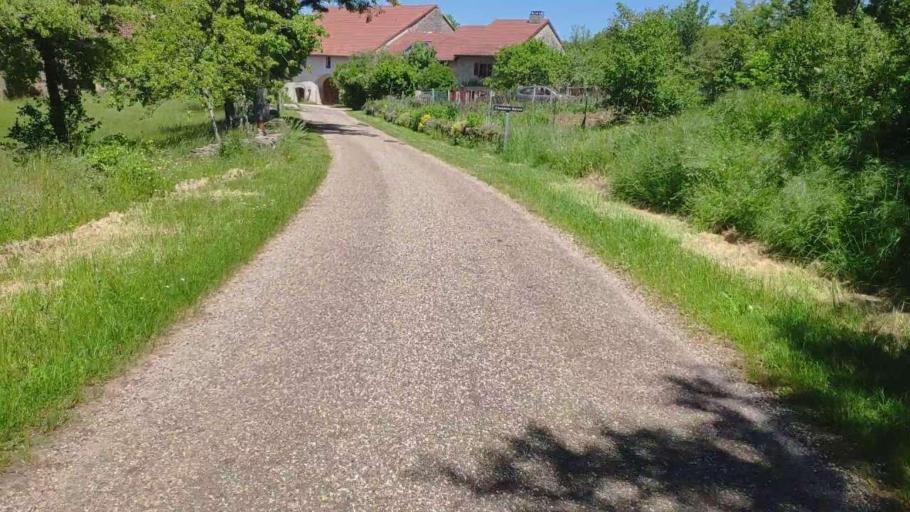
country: FR
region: Franche-Comte
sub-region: Departement du Jura
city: Poligny
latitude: 46.7426
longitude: 5.6735
